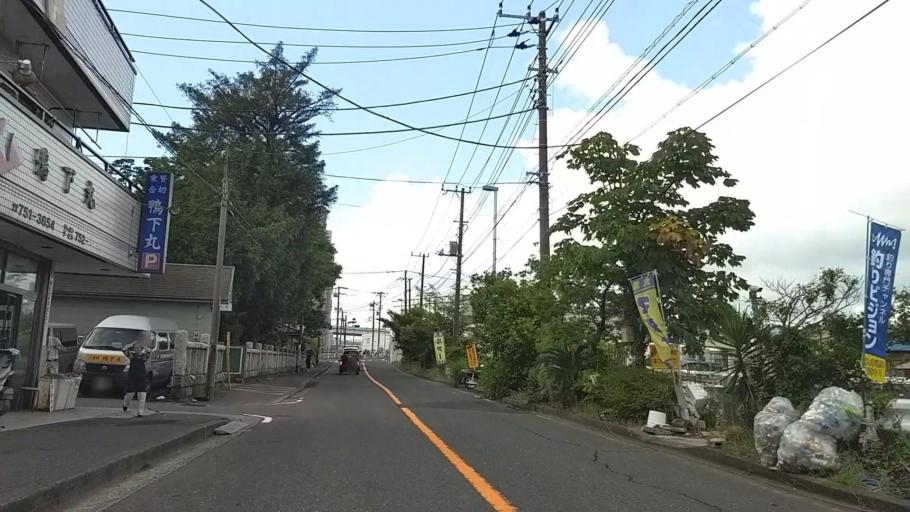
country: JP
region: Kanagawa
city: Yokohama
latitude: 35.4159
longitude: 139.6274
